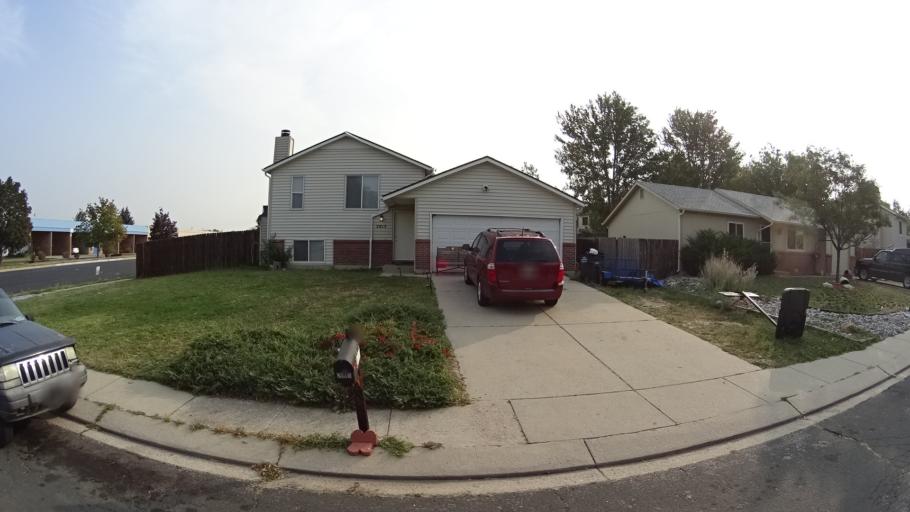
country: US
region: Colorado
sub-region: El Paso County
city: Stratmoor
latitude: 38.8025
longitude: -104.7479
